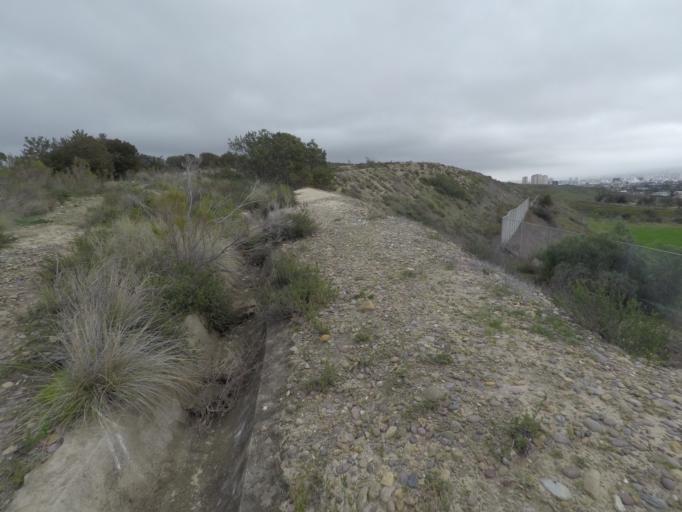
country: MX
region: Baja California
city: Tijuana
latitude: 32.5566
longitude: -117.0395
